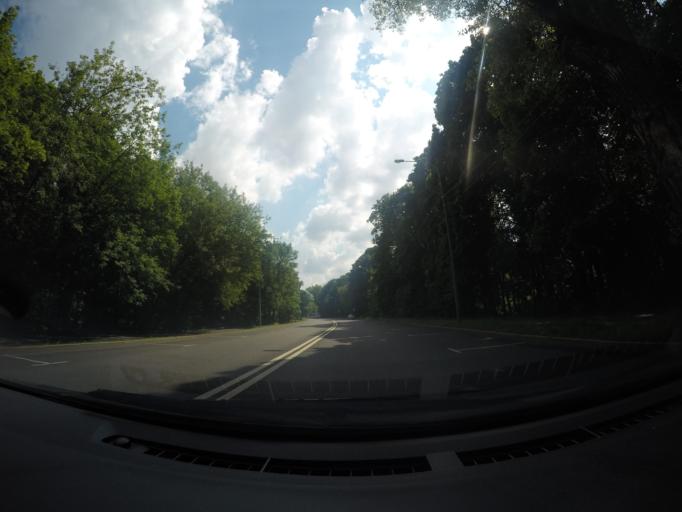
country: RU
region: Moscow
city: Sokol'niki
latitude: 55.8094
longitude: 37.6842
